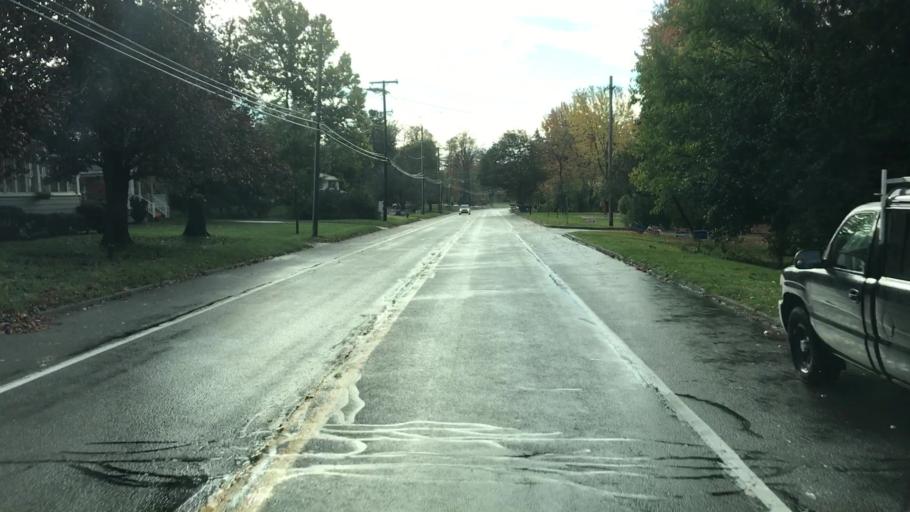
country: US
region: New York
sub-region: Onondaga County
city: Skaneateles
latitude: 42.9416
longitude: -76.4136
